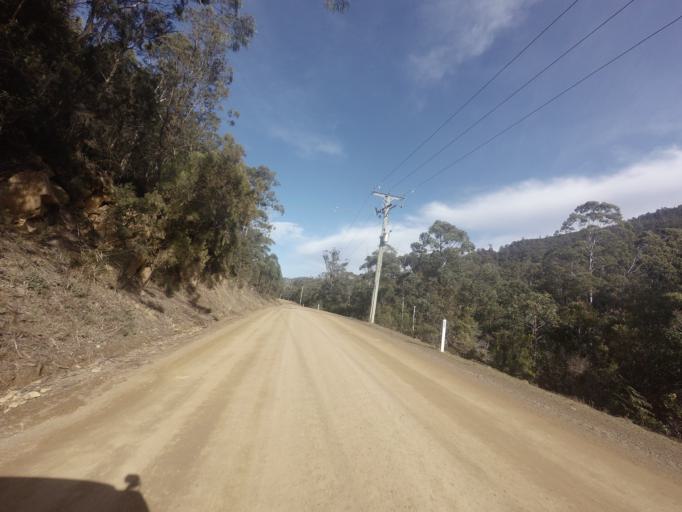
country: AU
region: Tasmania
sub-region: Huon Valley
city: Huonville
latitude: -43.0578
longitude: 147.0968
